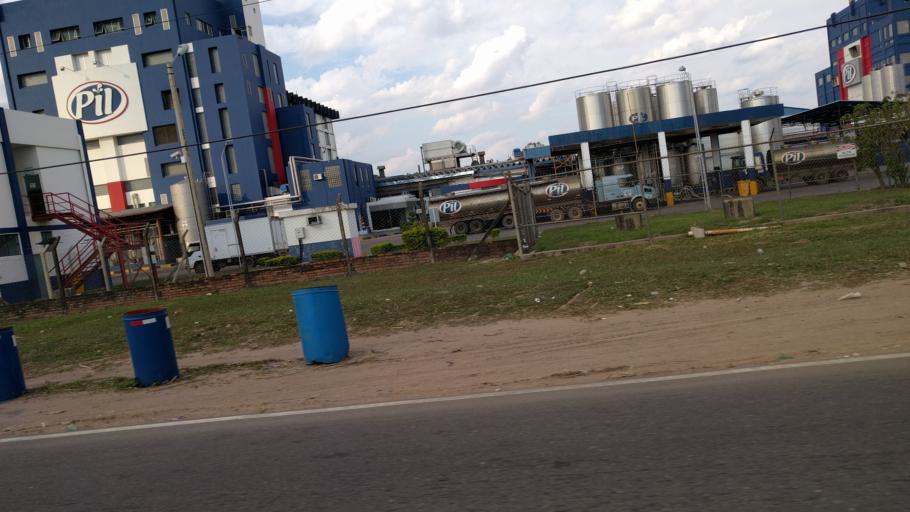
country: BO
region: Santa Cruz
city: Warnes
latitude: -17.5312
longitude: -63.1614
